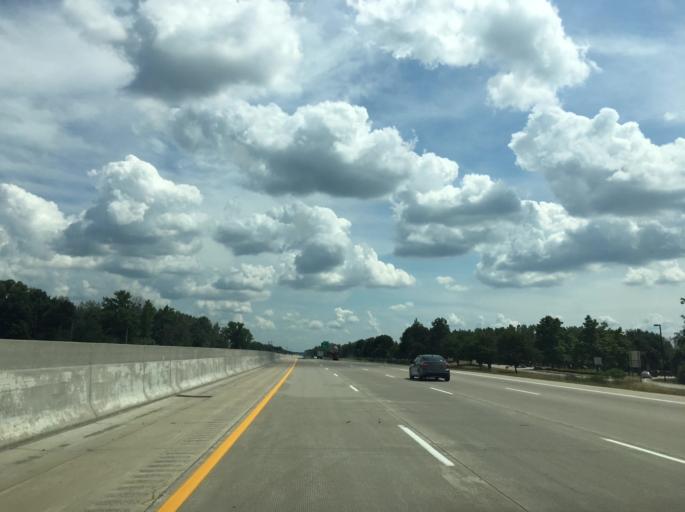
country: US
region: Michigan
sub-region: Saginaw County
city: Zilwaukee
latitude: 43.5311
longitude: -83.9436
